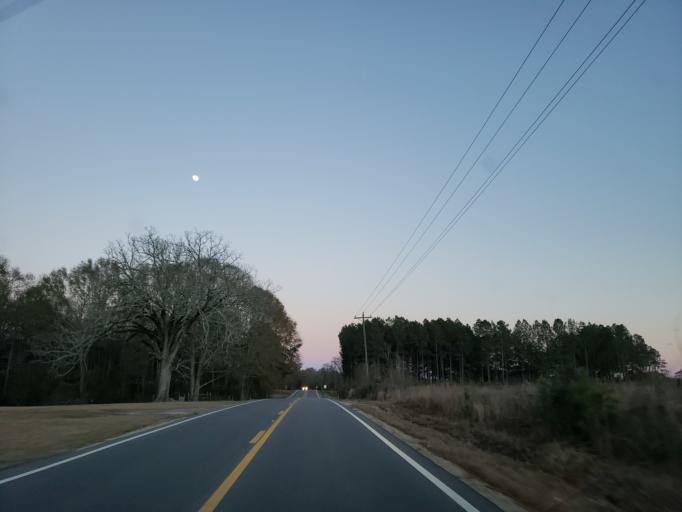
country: US
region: Mississippi
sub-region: Jones County
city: Ellisville
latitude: 31.5797
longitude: -89.2572
